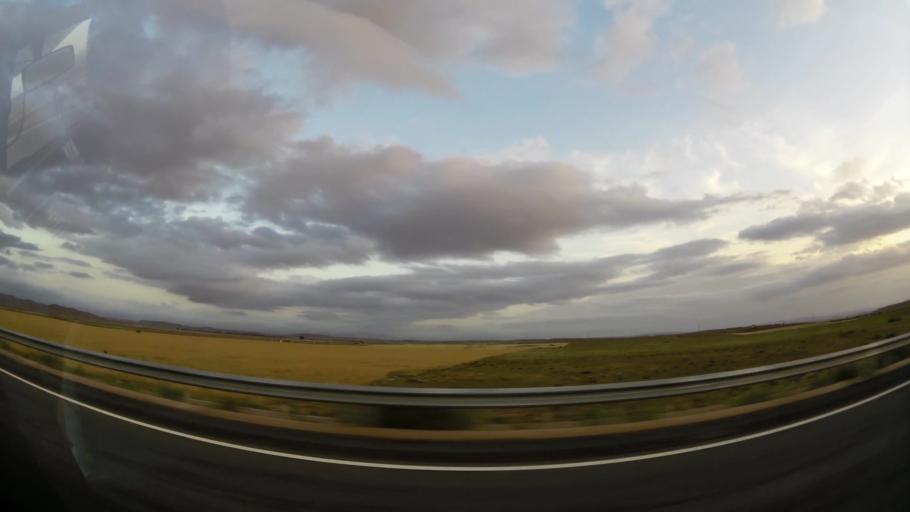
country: MA
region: Oriental
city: Taourirt
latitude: 34.6049
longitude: -2.7527
